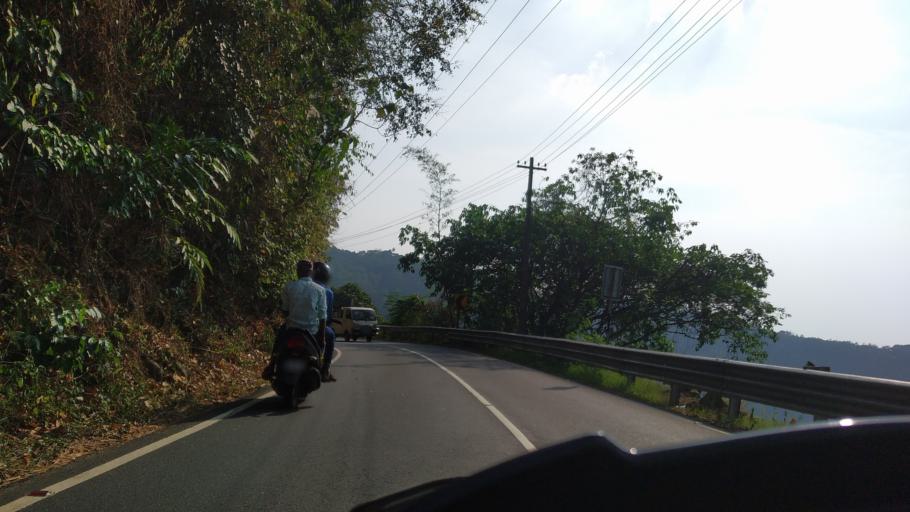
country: IN
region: Kerala
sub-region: Kottayam
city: Erattupetta
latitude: 9.5537
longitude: 76.9378
